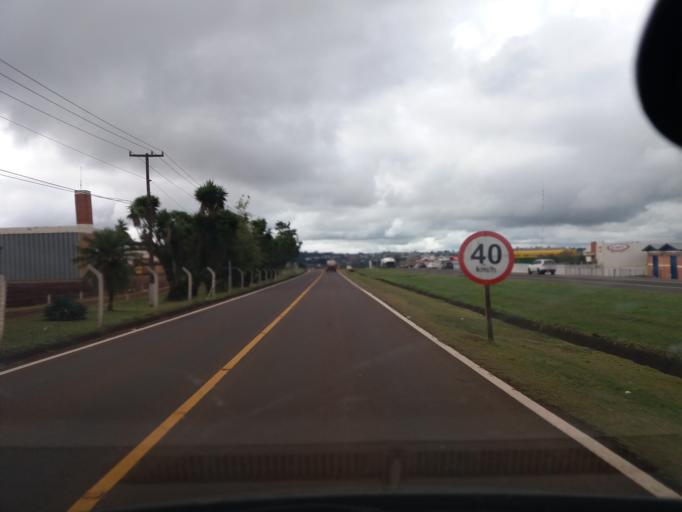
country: BR
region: Parana
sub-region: Cascavel
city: Cascavel
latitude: -24.9779
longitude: -53.4477
